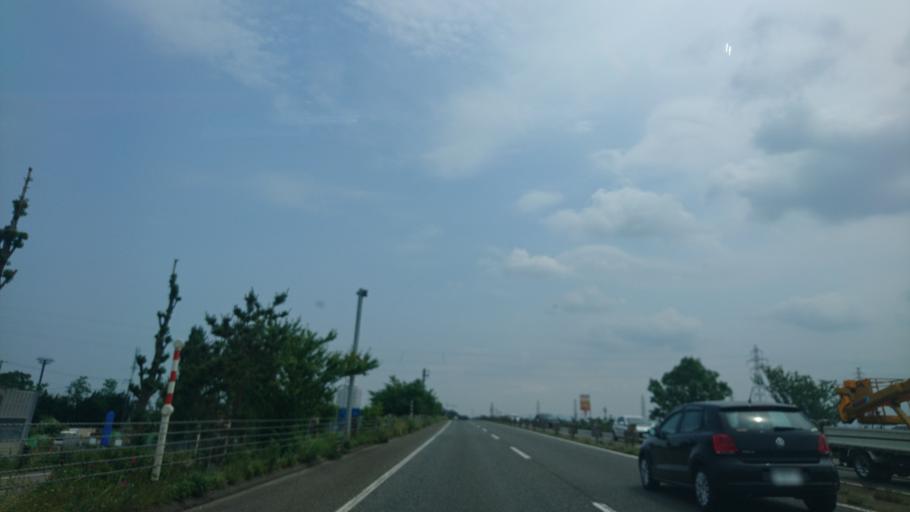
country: JP
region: Niigata
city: Kameda-honcho
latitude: 37.9414
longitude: 139.1816
